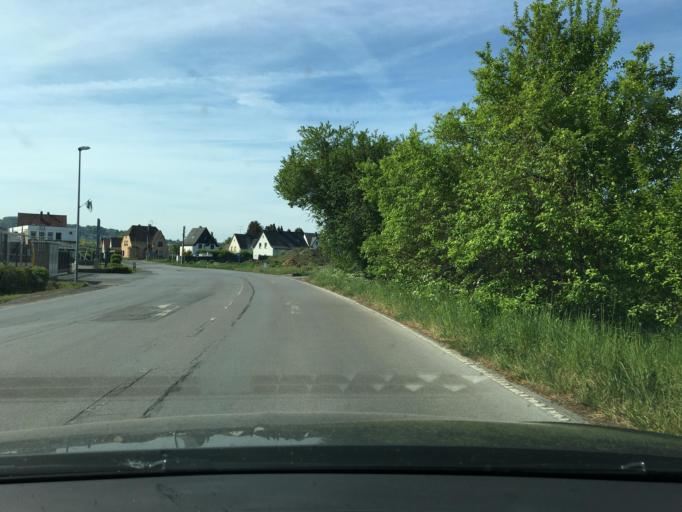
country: DE
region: North Rhine-Westphalia
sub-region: Regierungsbezirk Arnsberg
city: Frondenberg
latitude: 51.4806
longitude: 7.8041
